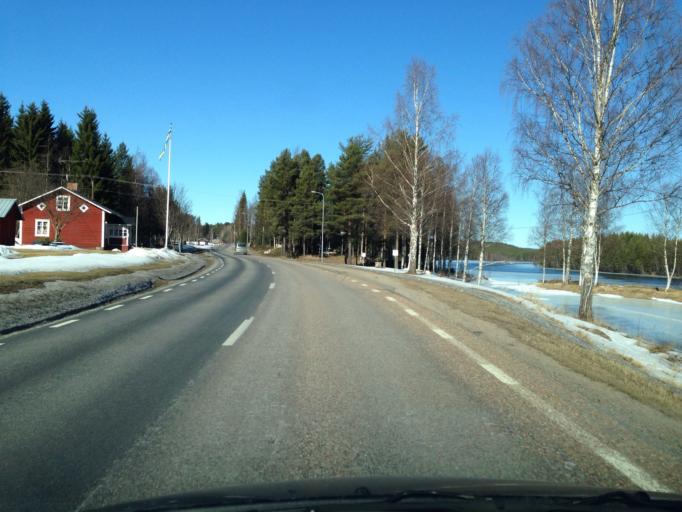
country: SE
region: Gaevleborg
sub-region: Ljusdals Kommun
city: Farila
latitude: 61.9768
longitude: 15.3301
